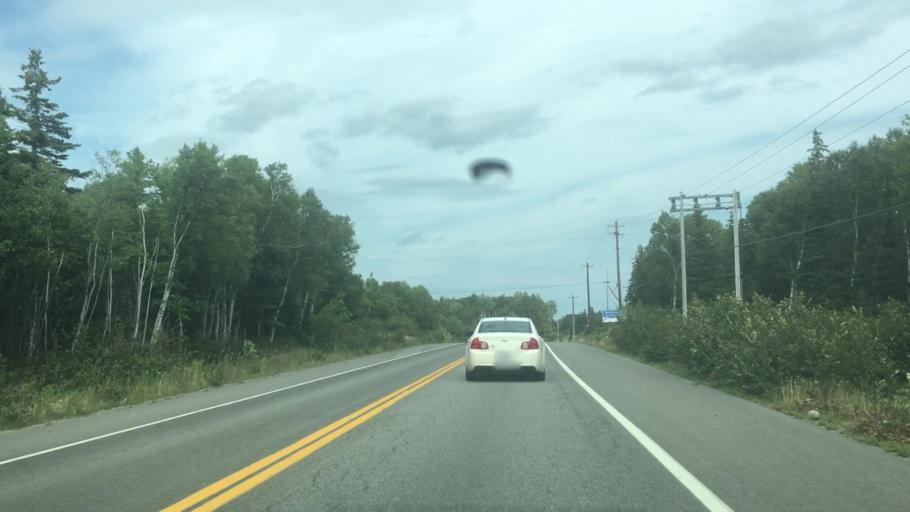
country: CA
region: Nova Scotia
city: Sydney Mines
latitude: 46.5203
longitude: -60.4230
